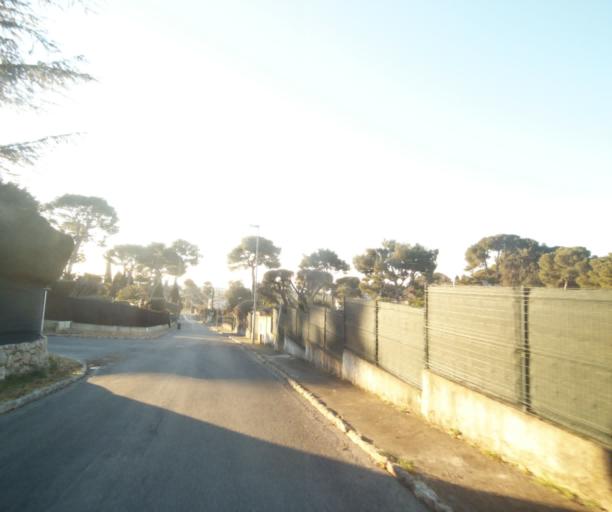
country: FR
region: Provence-Alpes-Cote d'Azur
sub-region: Departement des Alpes-Maritimes
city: Vallauris
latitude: 43.5813
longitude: 7.0824
